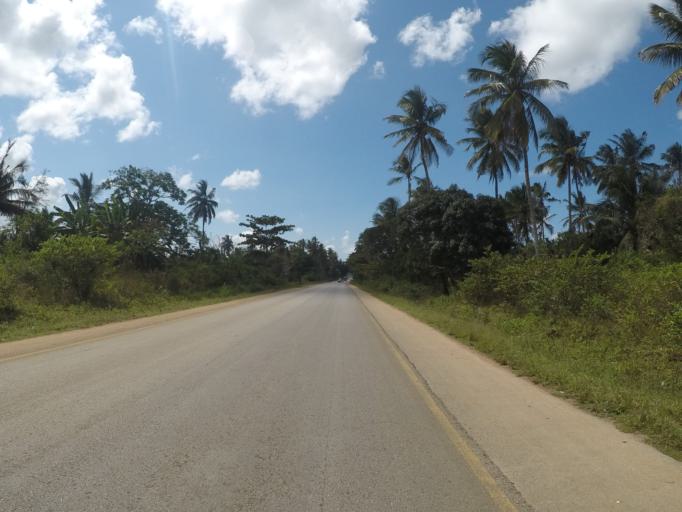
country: TZ
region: Zanzibar Central/South
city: Koani
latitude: -6.1574
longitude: 39.3297
